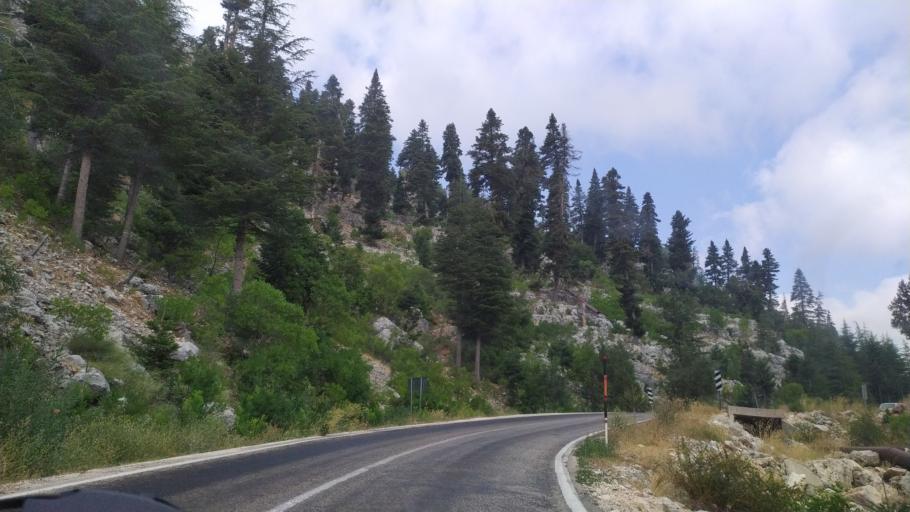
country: TR
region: Mersin
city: Kirobasi
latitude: 36.6068
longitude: 33.8842
